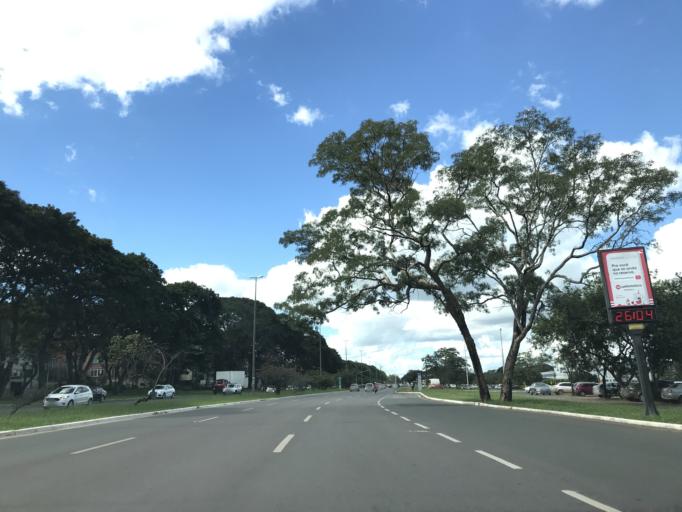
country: BR
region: Federal District
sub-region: Brasilia
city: Brasilia
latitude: -15.8265
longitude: -47.9025
